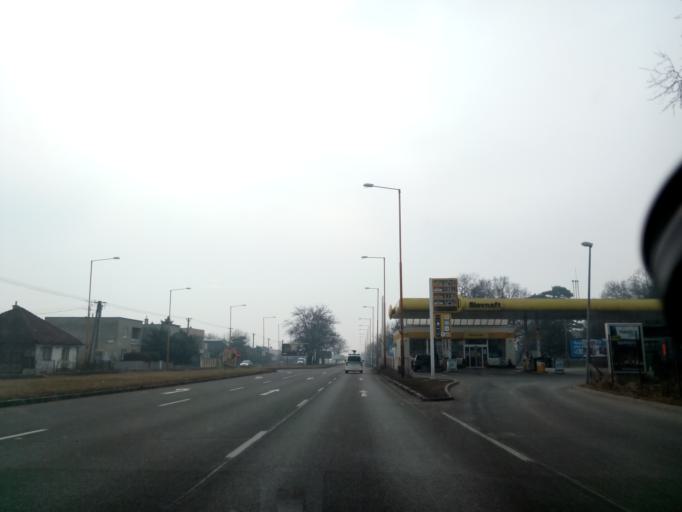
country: SK
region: Kosicky
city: Kosice
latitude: 48.6785
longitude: 21.2687
